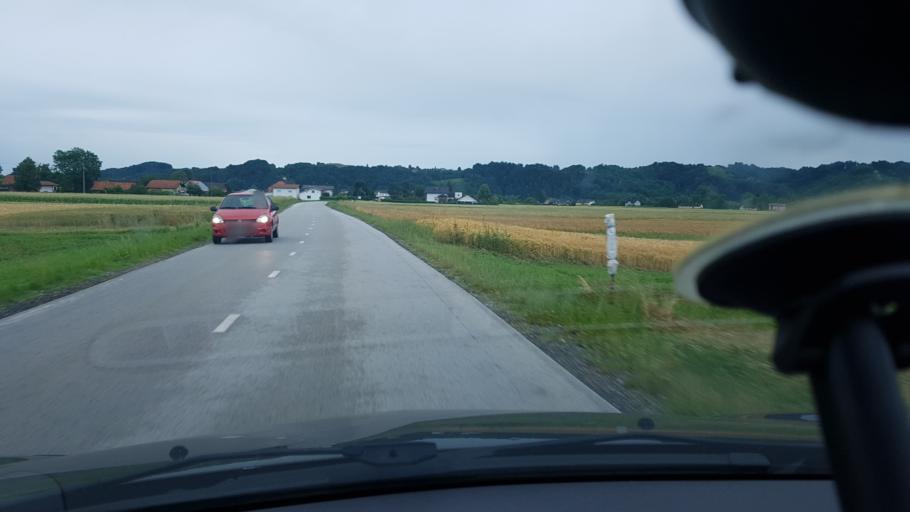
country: SI
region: Videm
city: Videm pri Ptuju
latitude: 46.3764
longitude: 15.8861
